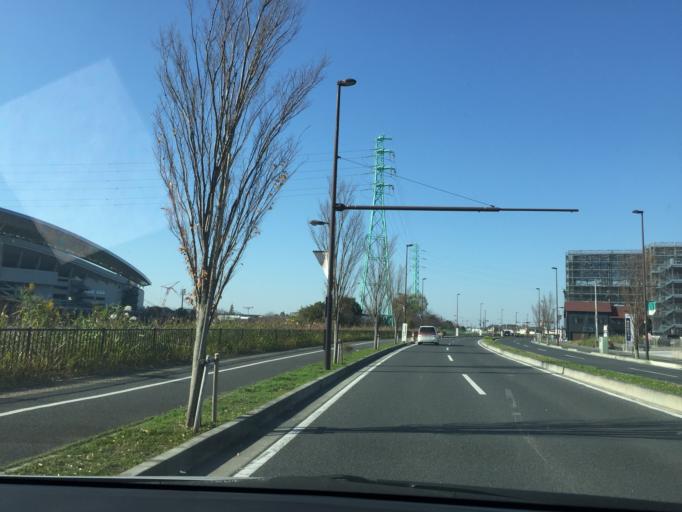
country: JP
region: Saitama
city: Iwatsuki
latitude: 35.9031
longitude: 139.7225
